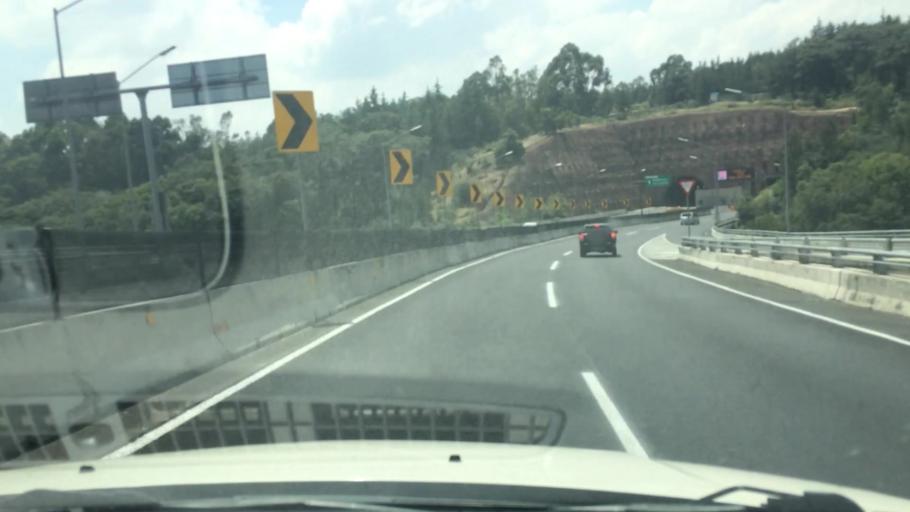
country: MX
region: Mexico City
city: Magdalena Contreras
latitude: 19.3324
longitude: -99.2373
